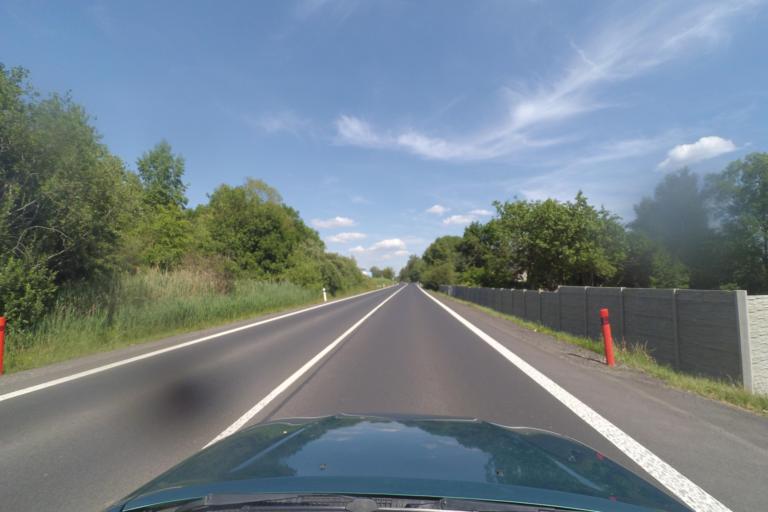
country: CZ
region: Liberecky
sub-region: Okres Ceska Lipa
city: Ceska Lipa
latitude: 50.6813
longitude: 14.5692
